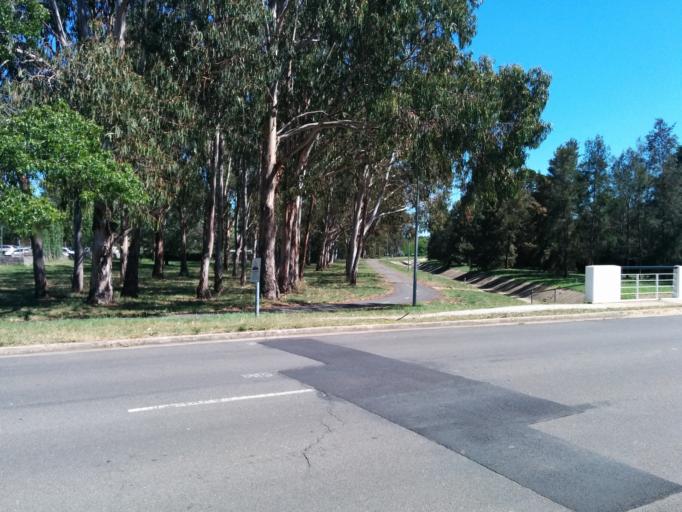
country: AU
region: Australian Capital Territory
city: Acton
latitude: -35.2559
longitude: 149.1288
